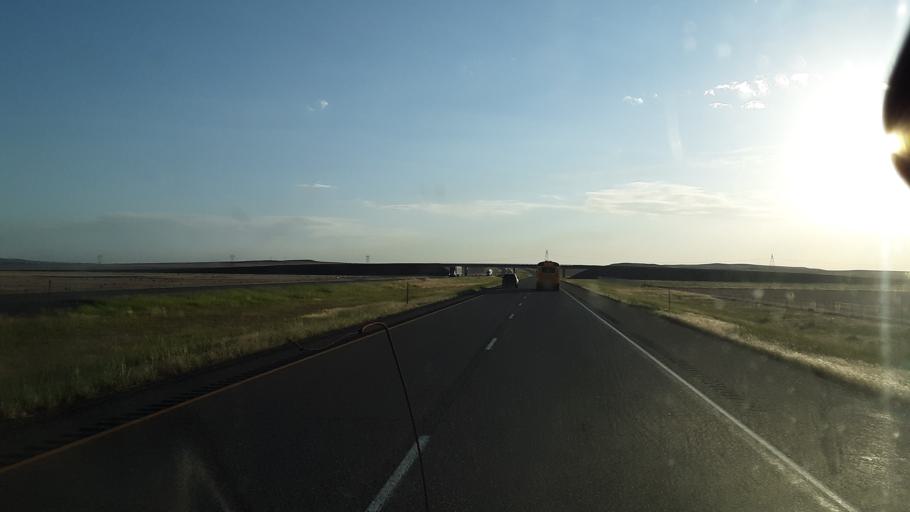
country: US
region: Montana
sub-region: Big Horn County
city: Hardin
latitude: 45.7464
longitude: -107.6767
